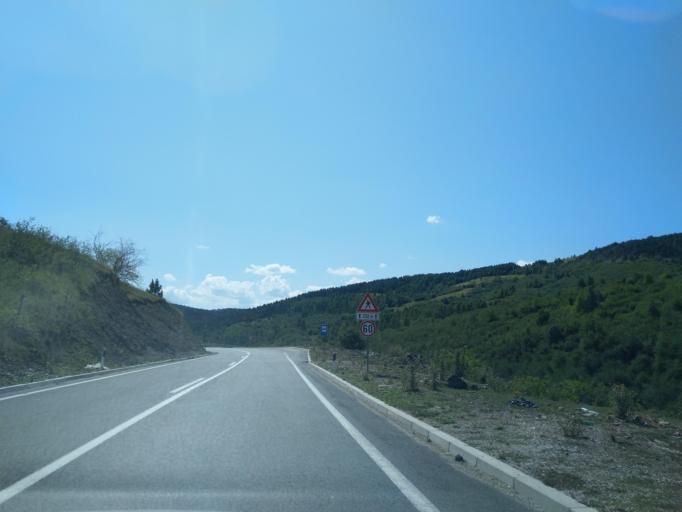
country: RS
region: Central Serbia
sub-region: Zlatiborski Okrug
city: Sjenica
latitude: 43.2875
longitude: 19.9434
